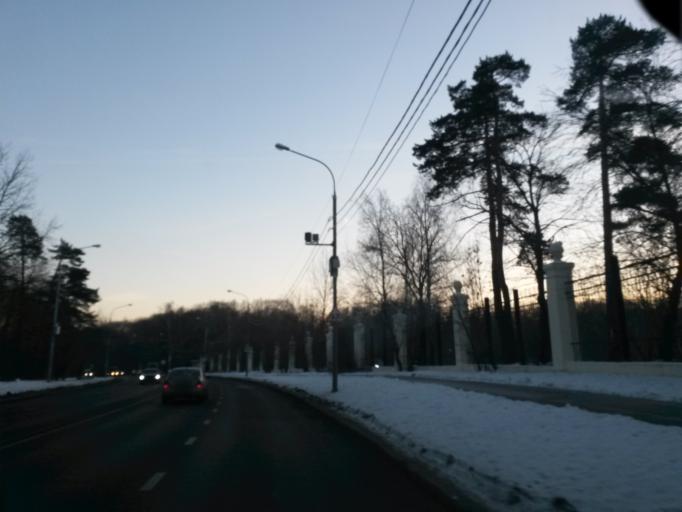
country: RU
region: Moscow
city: Sokol'niki
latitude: 55.8046
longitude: 37.6839
